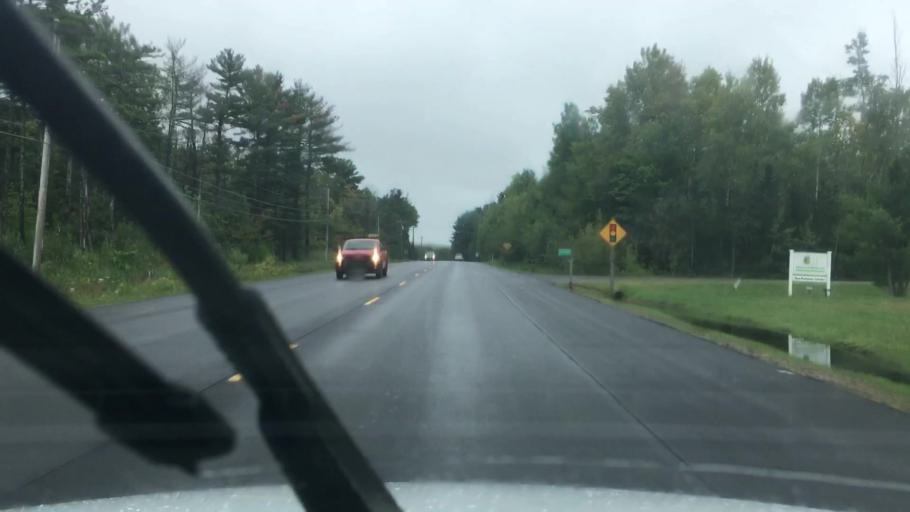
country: US
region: Maine
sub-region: Penobscot County
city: Hampden
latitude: 44.7574
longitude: -68.8438
